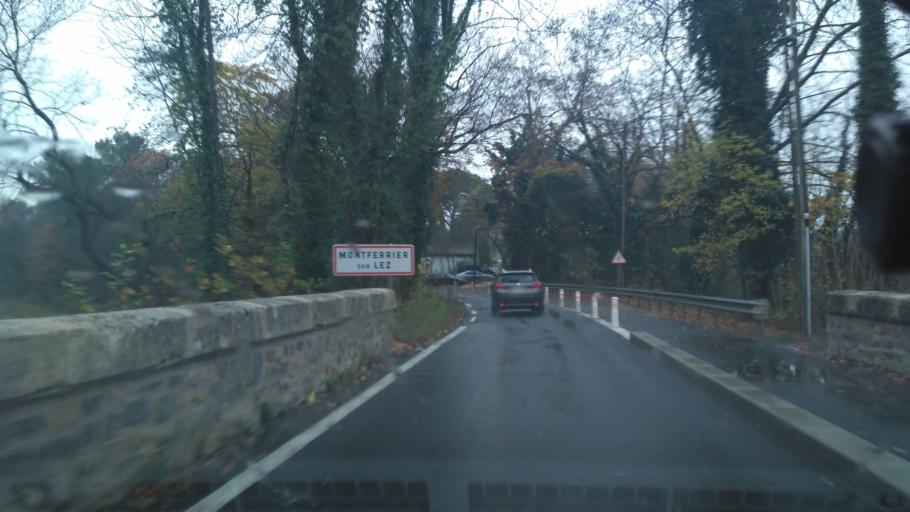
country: FR
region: Languedoc-Roussillon
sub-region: Departement de l'Herault
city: Clapiers
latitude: 43.6479
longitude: 3.8686
